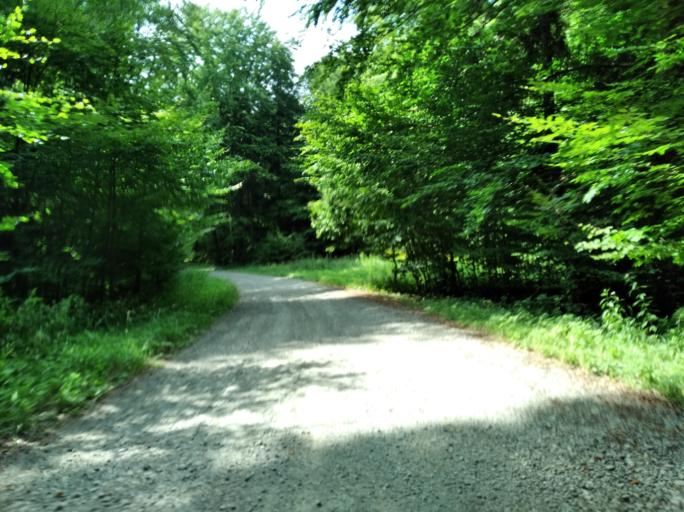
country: PL
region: Subcarpathian Voivodeship
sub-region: Powiat krosnienski
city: Leki
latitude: 49.8393
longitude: 21.6634
